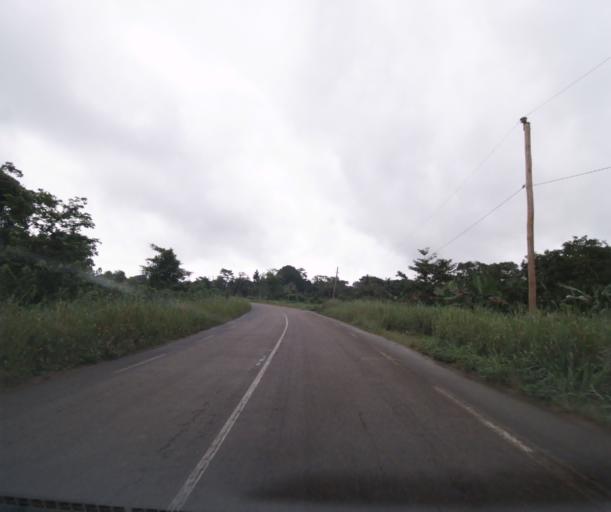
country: CM
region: Littoral
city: Dizangue
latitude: 3.4986
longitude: 10.1176
